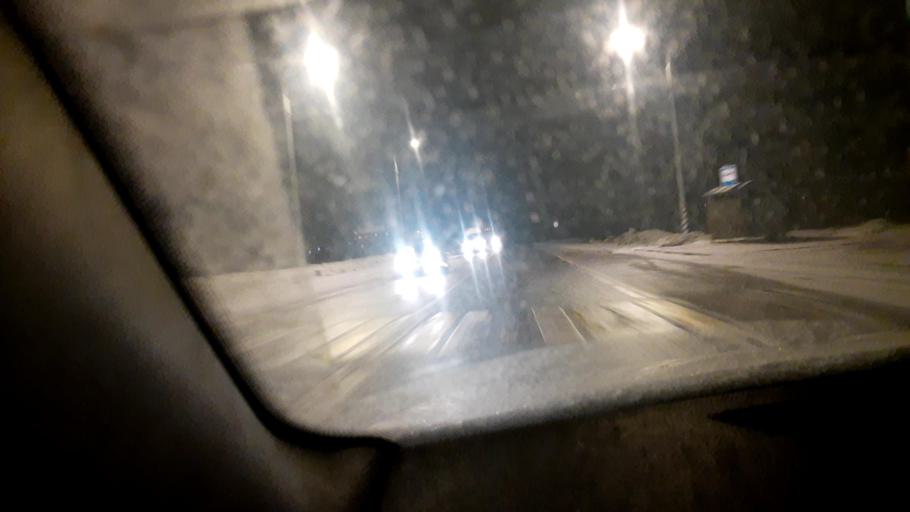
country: RU
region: Moskovskaya
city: Skoropuskovskiy
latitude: 56.4018
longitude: 38.1069
